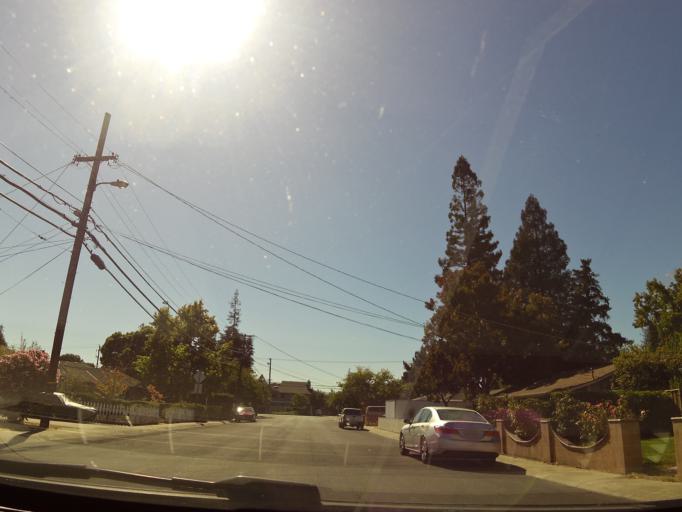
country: US
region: California
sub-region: Santa Clara County
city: Campbell
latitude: 37.2880
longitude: -121.9574
